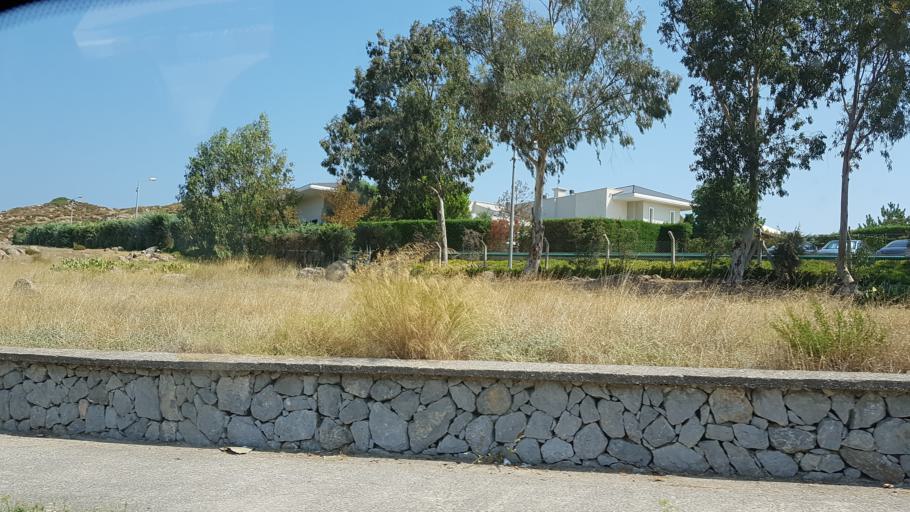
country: TR
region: Izmir
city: Urla
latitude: 38.3805
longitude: 26.7585
